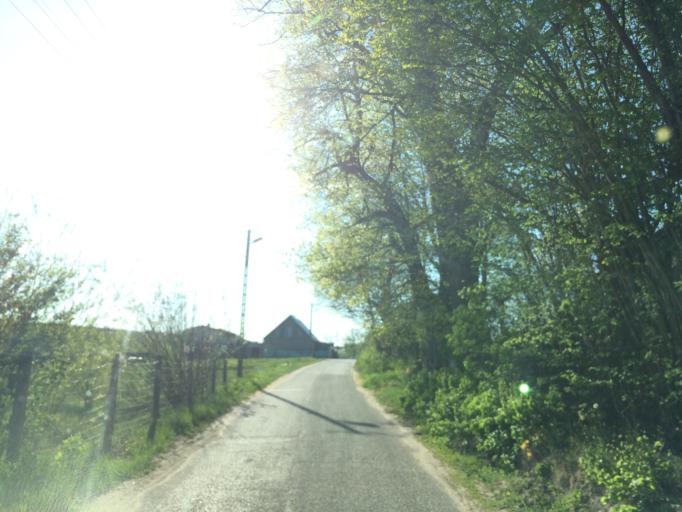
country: PL
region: Warmian-Masurian Voivodeship
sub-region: Powiat dzialdowski
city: Lidzbark
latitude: 53.2389
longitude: 19.7601
